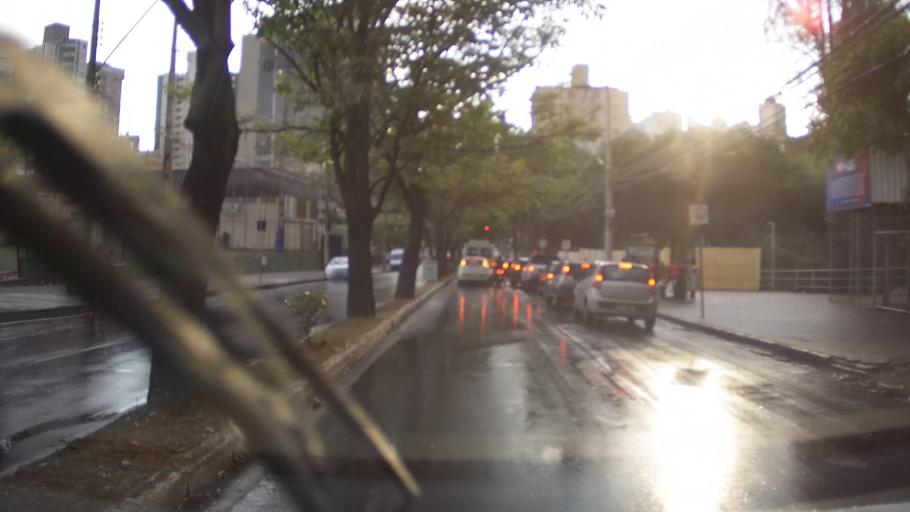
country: BR
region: Minas Gerais
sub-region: Belo Horizonte
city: Belo Horizonte
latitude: -19.9674
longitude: -43.9621
